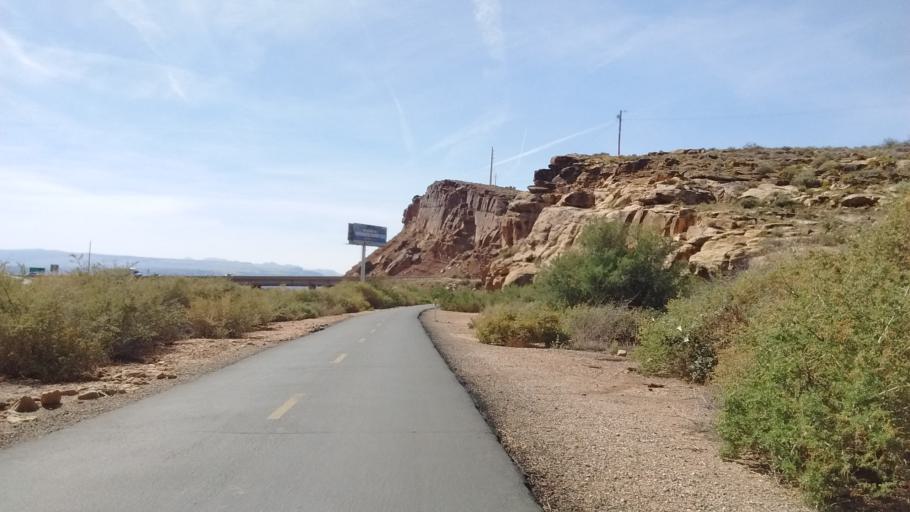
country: US
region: Utah
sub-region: Washington County
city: Saint George
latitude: 37.0716
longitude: -113.5820
